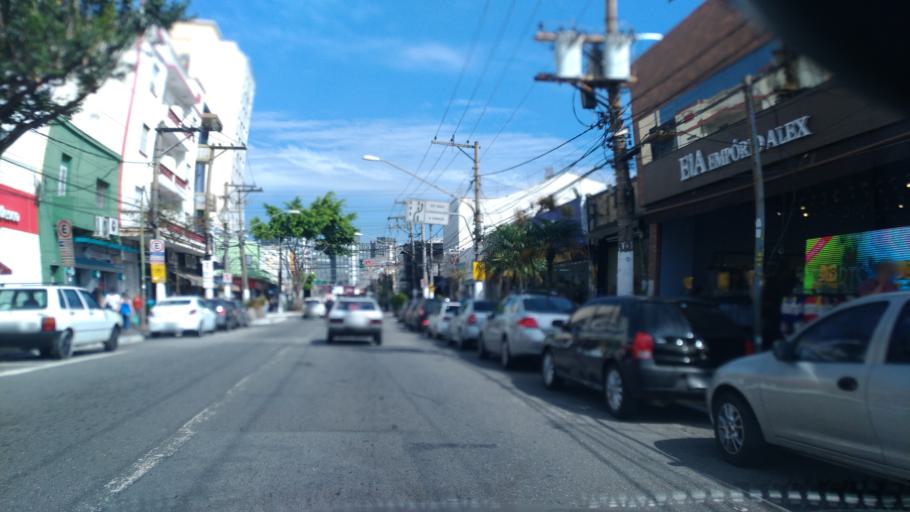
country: BR
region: Sao Paulo
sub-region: Sao Caetano Do Sul
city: Sao Caetano do Sul
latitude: -23.5985
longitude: -46.6007
